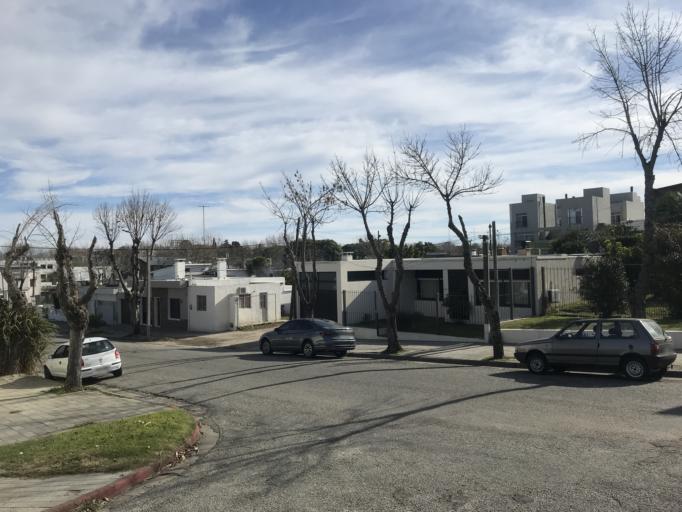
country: UY
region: Colonia
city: Colonia del Sacramento
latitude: -34.4694
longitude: -57.8397
